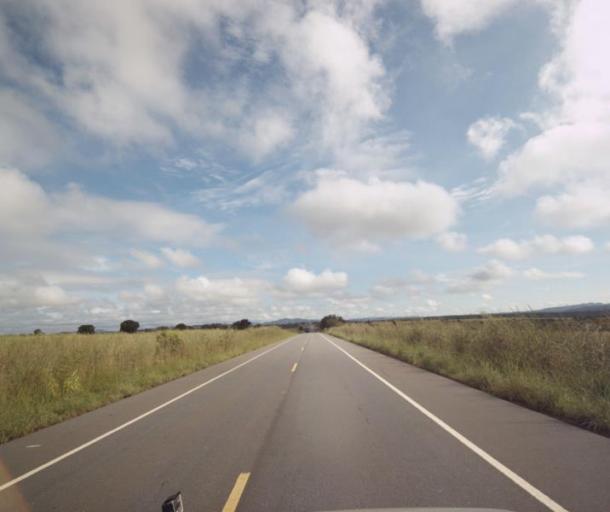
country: BR
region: Goias
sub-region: Barro Alto
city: Barro Alto
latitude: -15.2404
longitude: -48.6914
